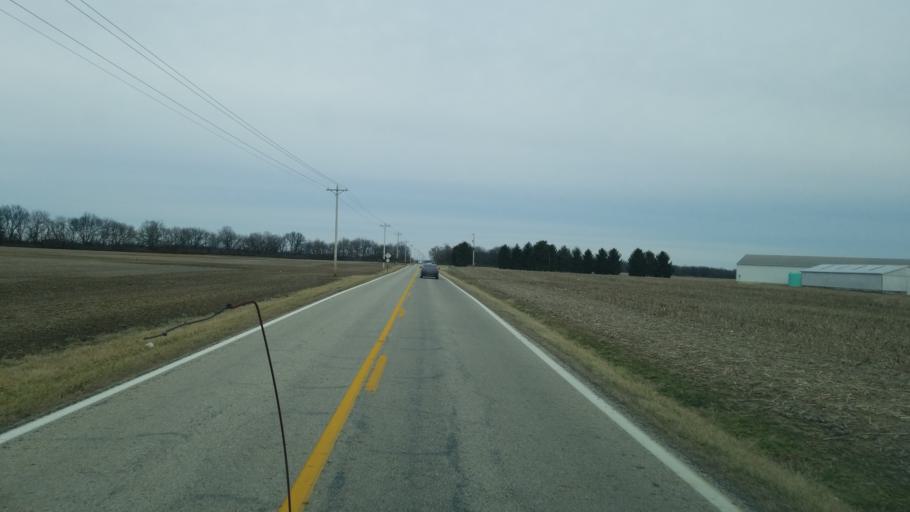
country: US
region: Ohio
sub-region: Pickaway County
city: Williamsport
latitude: 39.5749
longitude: -83.0441
